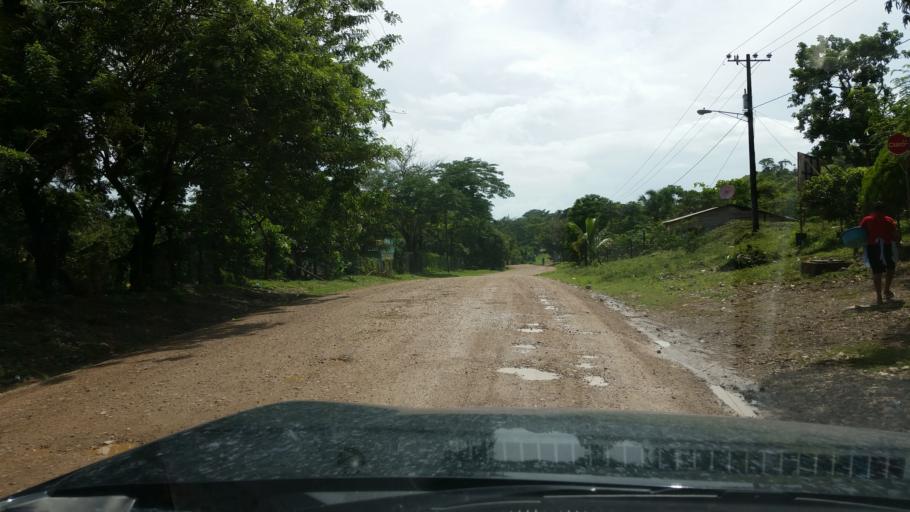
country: NI
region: Atlantico Norte (RAAN)
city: Siuna
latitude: 13.6814
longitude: -84.6480
